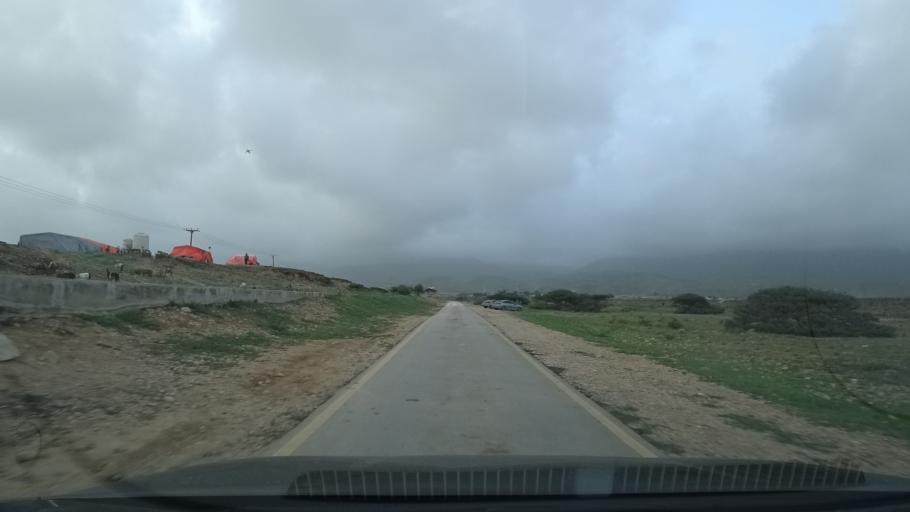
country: OM
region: Zufar
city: Salalah
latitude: 17.0912
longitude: 54.2330
